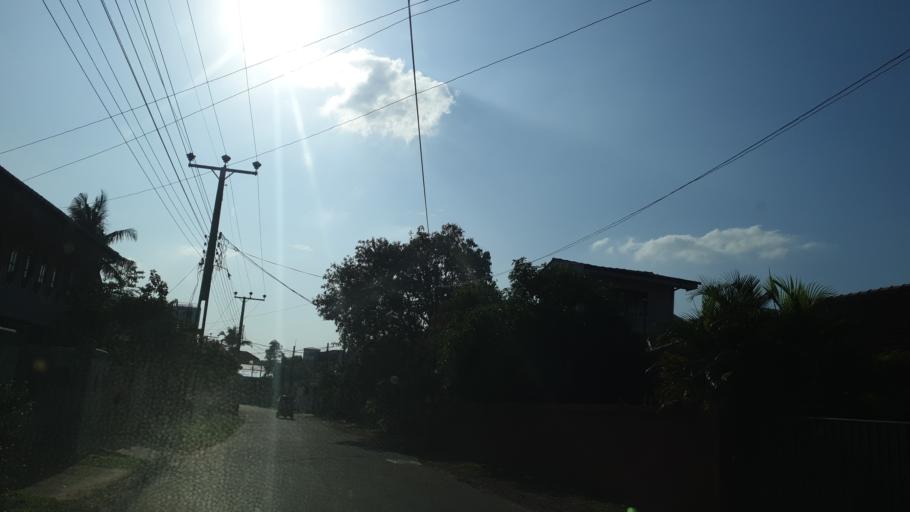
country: LK
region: Western
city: Battaramulla South
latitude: 6.8821
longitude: 79.9382
